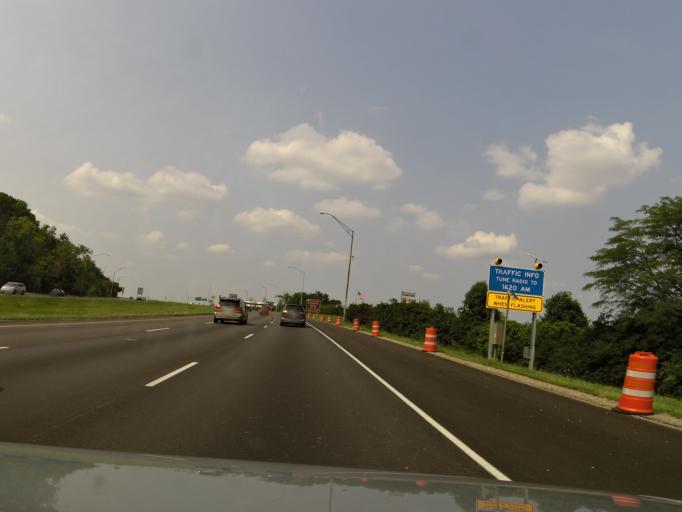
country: US
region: Ohio
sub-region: Hamilton County
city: Glendale
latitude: 39.2604
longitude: -84.4405
